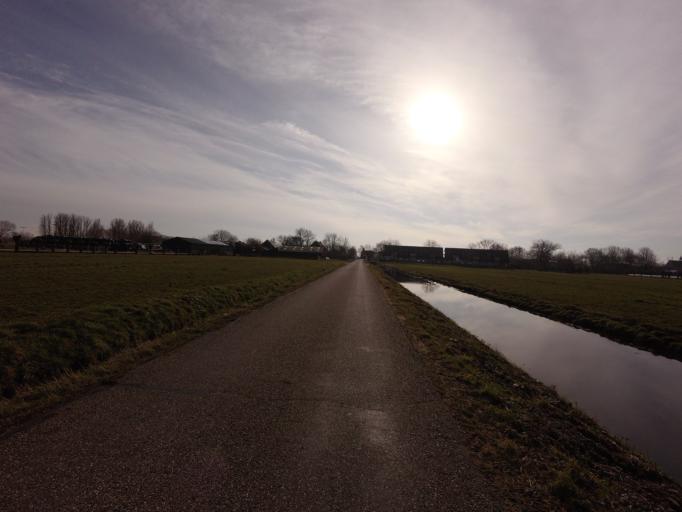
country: NL
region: South Holland
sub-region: Gemeente Sliedrecht
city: Sliedrecht
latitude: 51.8473
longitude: 4.7679
